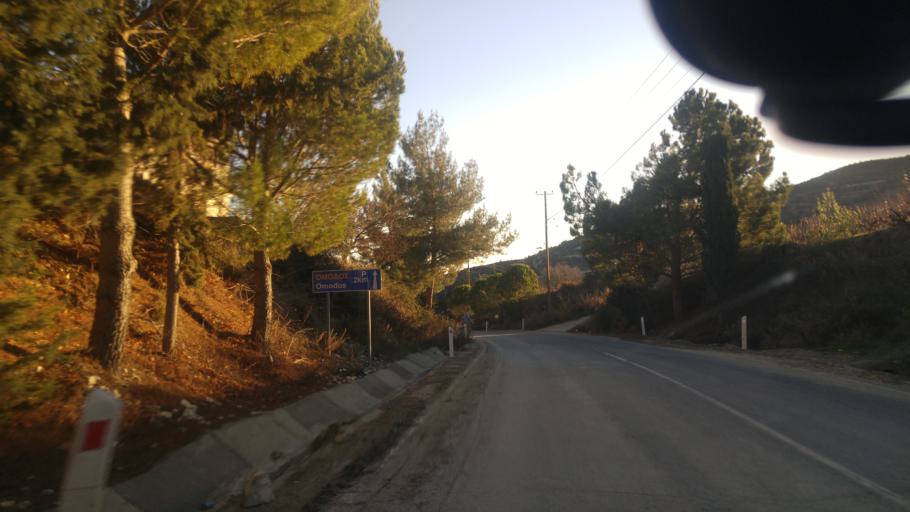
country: CY
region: Limassol
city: Pachna
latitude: 34.8536
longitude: 32.8067
